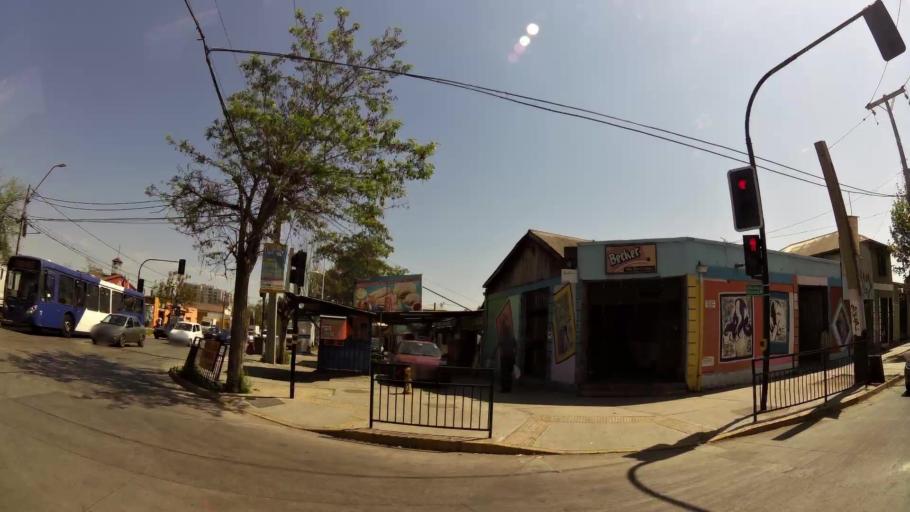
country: CL
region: Santiago Metropolitan
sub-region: Provincia de Santiago
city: La Pintana
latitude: -33.5447
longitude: -70.6520
